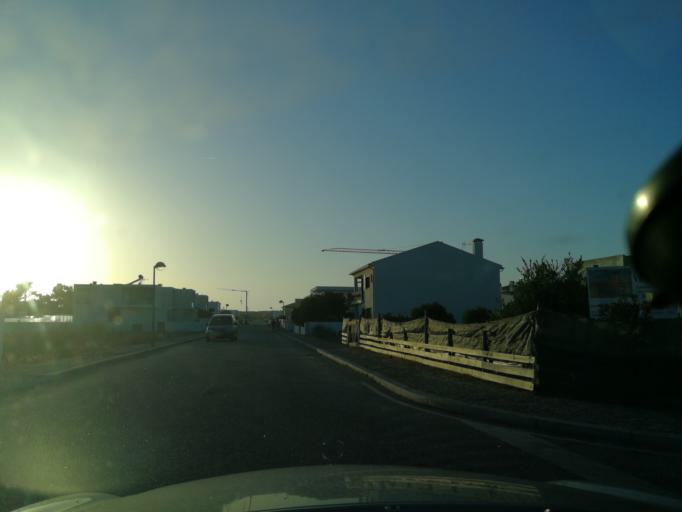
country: PT
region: Aveiro
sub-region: Murtosa
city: Murtosa
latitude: 40.7568
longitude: -8.7064
